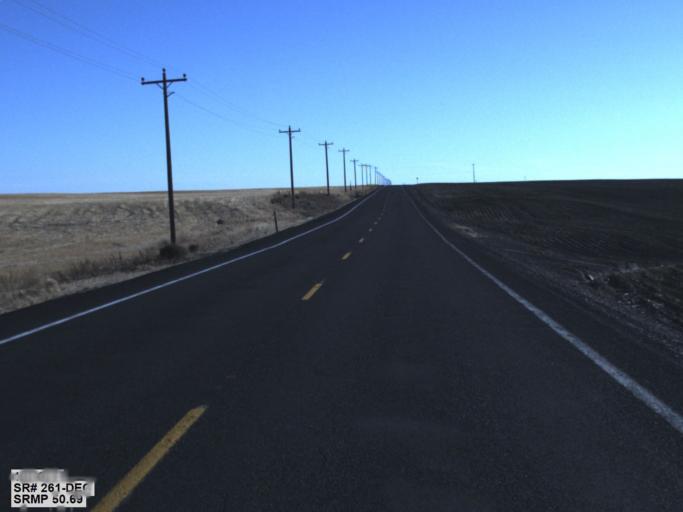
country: US
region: Washington
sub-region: Adams County
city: Ritzville
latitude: 46.9473
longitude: -118.3434
